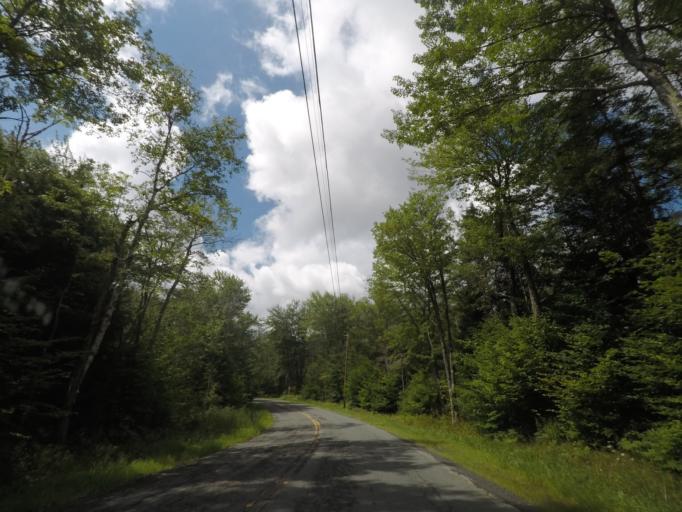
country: US
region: New York
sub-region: Rensselaer County
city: Averill Park
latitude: 42.6473
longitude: -73.4311
